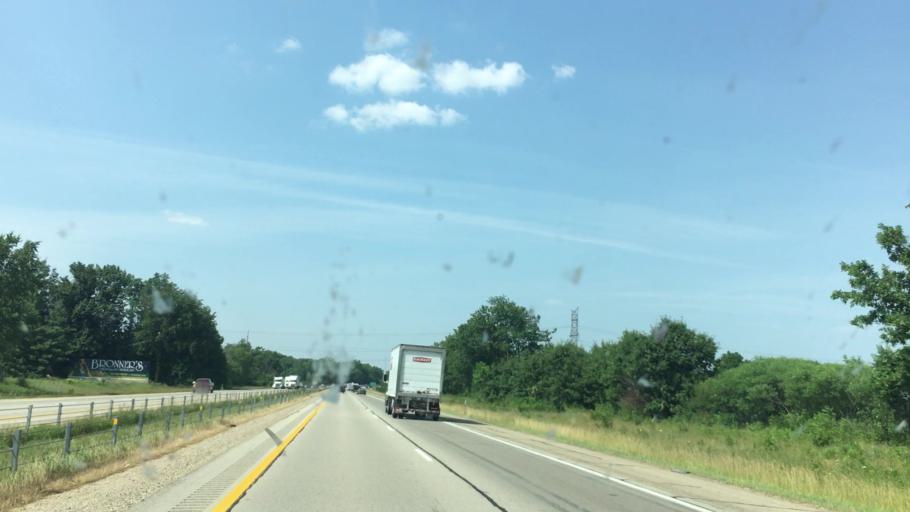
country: US
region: Michigan
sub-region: Kent County
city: Byron Center
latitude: 42.7559
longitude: -85.6735
